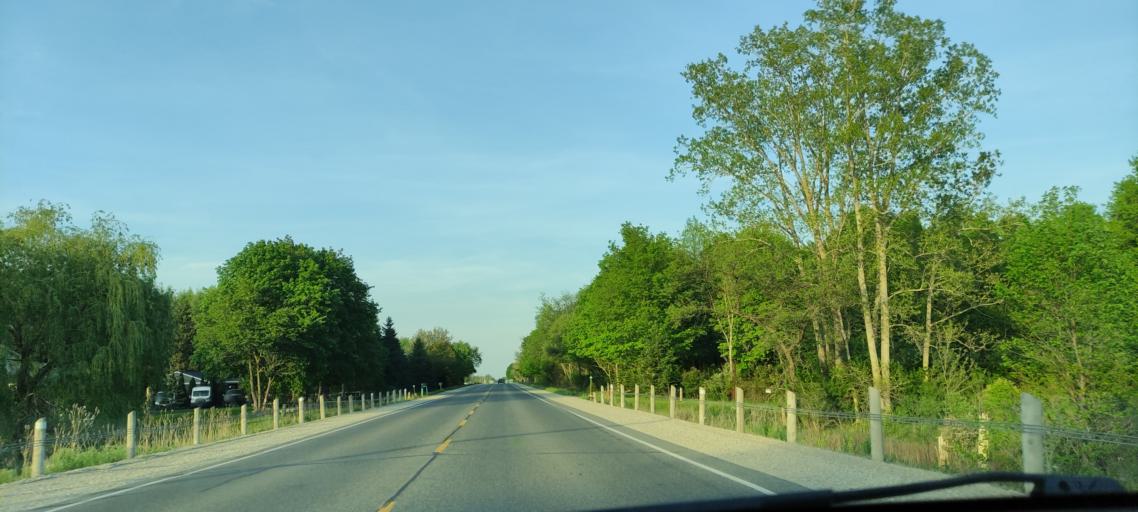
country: CA
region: Ontario
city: London
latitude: 43.1793
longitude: -81.3102
